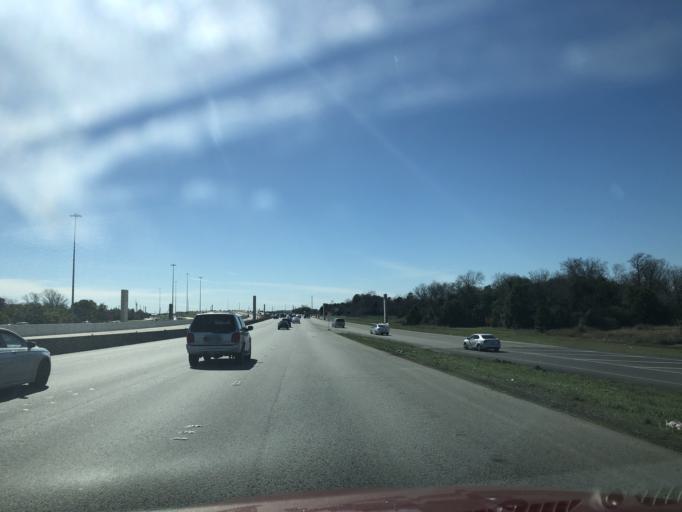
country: US
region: Texas
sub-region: Harris County
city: Southside Place
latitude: 29.6657
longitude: -95.3847
